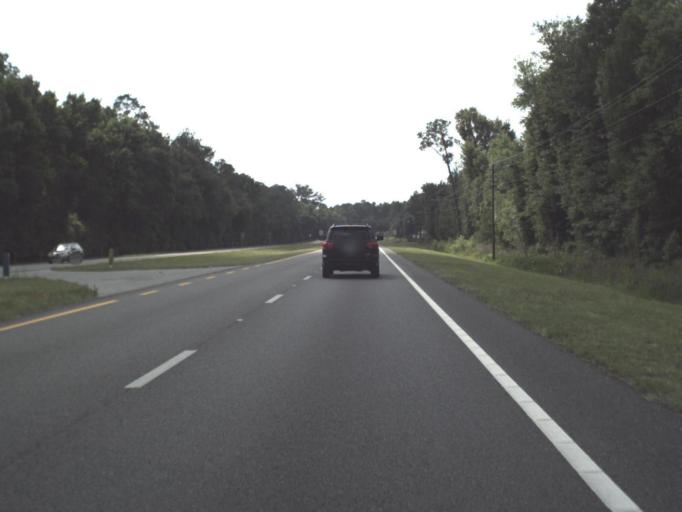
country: US
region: Florida
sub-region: Alachua County
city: Waldo
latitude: 29.7767
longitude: -82.1617
